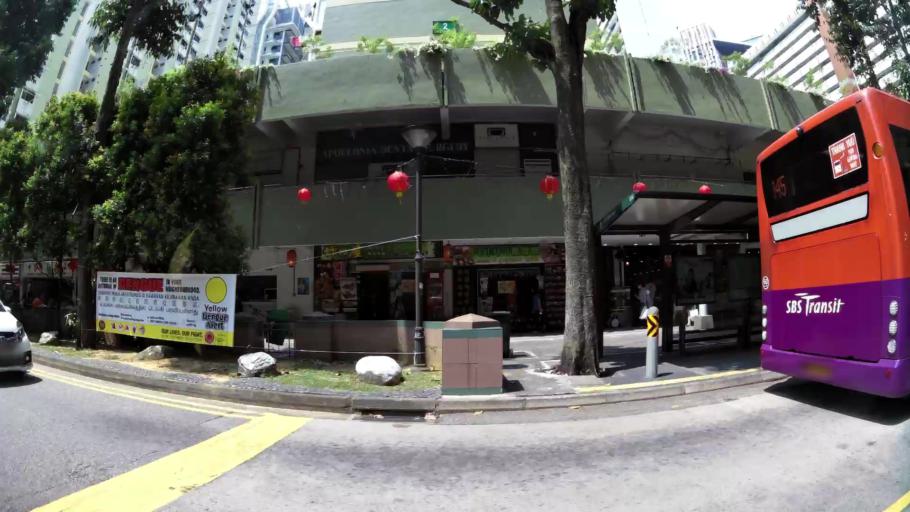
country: SG
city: Singapore
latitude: 1.2751
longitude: 103.8430
